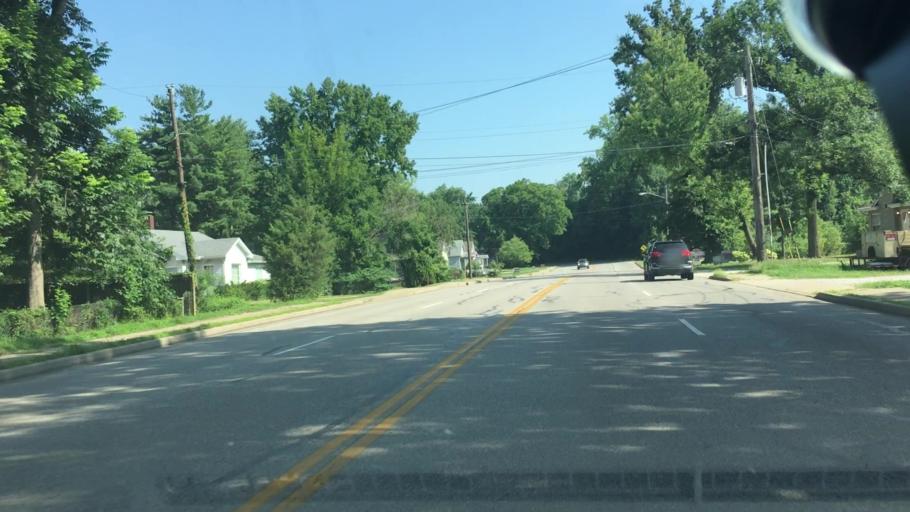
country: US
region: Indiana
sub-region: Vanderburgh County
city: Melody Hill
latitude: 37.9956
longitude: -87.5291
